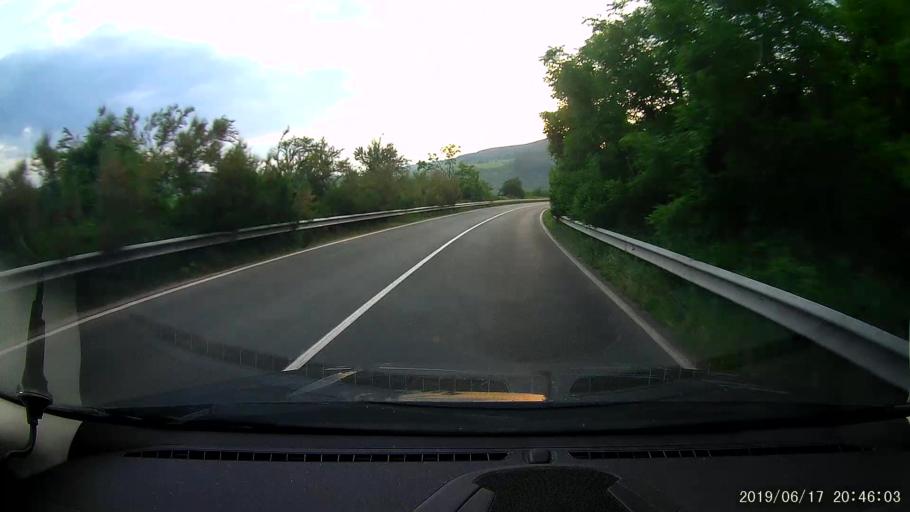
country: BG
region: Sofiya
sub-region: Obshtina Dragoman
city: Dragoman
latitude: 42.9375
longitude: 22.9090
